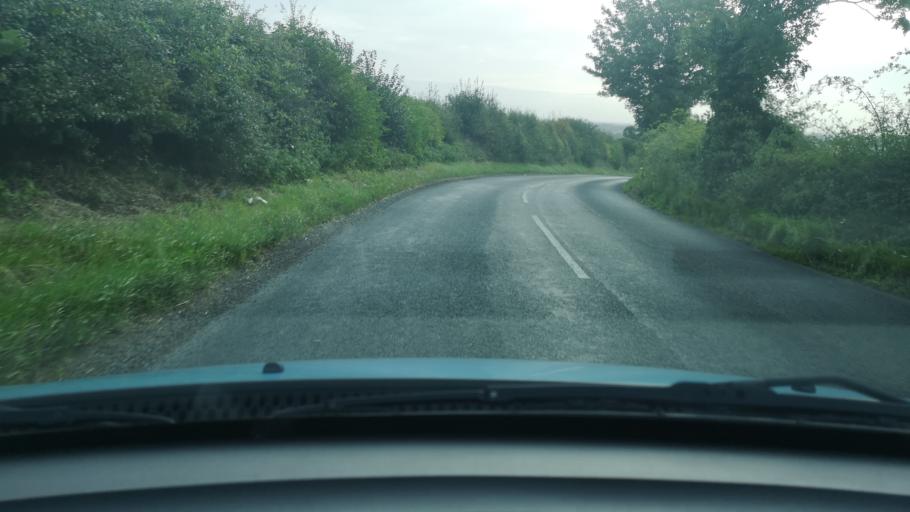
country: GB
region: England
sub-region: Doncaster
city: Campsall
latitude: 53.6177
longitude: -1.2020
